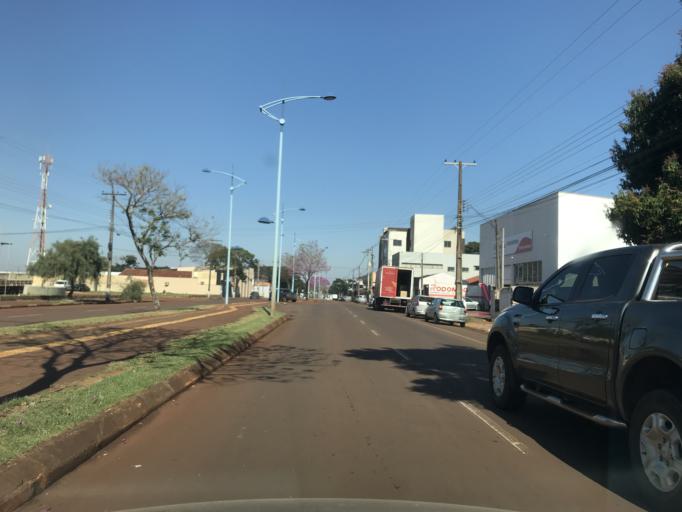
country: BR
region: Parana
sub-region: Toledo
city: Toledo
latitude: -24.7231
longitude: -53.7209
